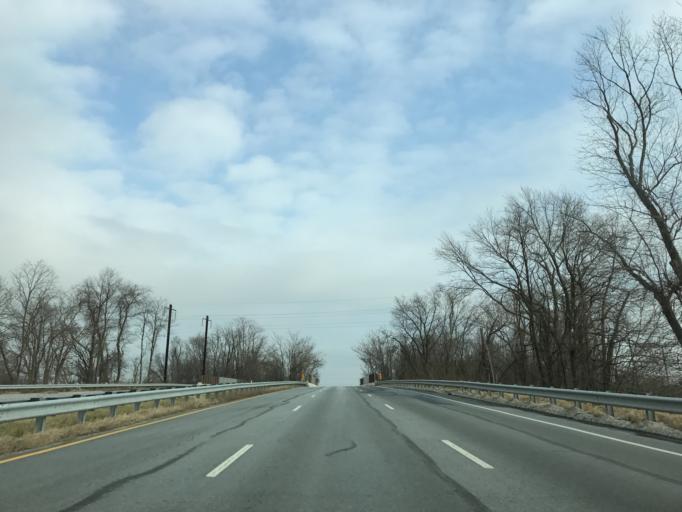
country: US
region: Maryland
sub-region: Harford County
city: Aberdeen
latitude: 39.4912
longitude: -76.1769
